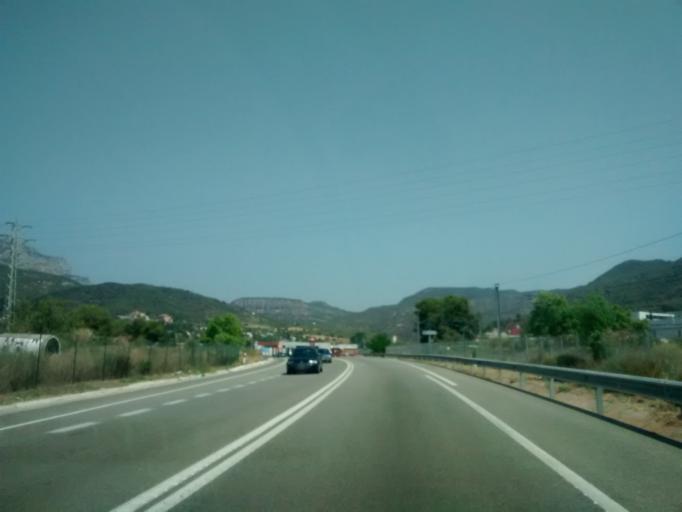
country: ES
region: Catalonia
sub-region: Provincia de Barcelona
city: Olesa de Montserrat
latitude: 41.5496
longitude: 1.8812
